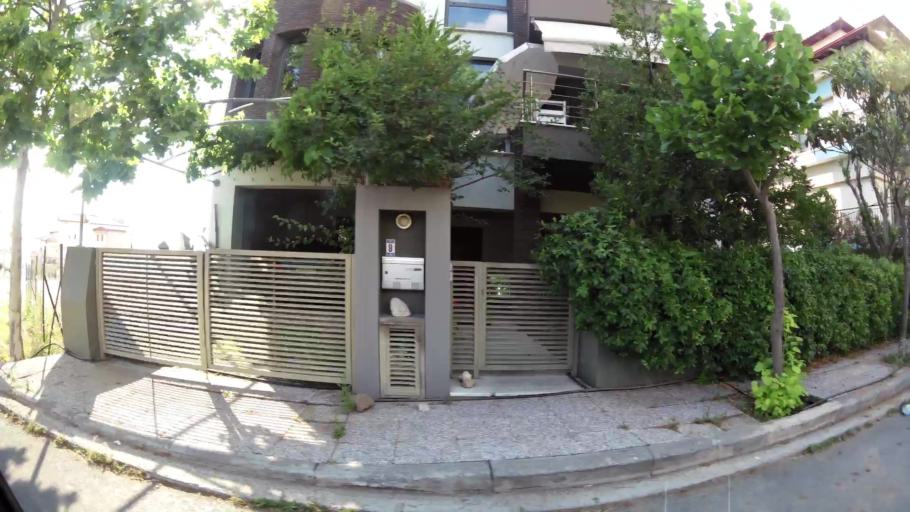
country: GR
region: Central Macedonia
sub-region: Nomos Thessalonikis
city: Polichni
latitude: 40.6603
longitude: 22.9545
